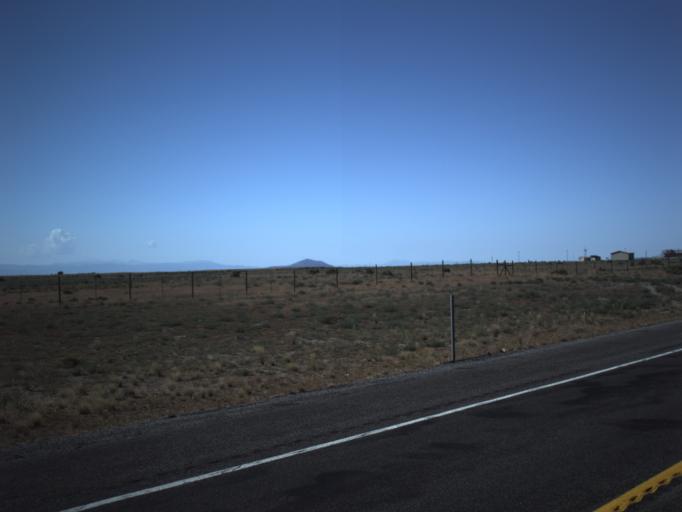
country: US
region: Utah
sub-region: Millard County
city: Delta
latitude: 39.3933
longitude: -112.5079
